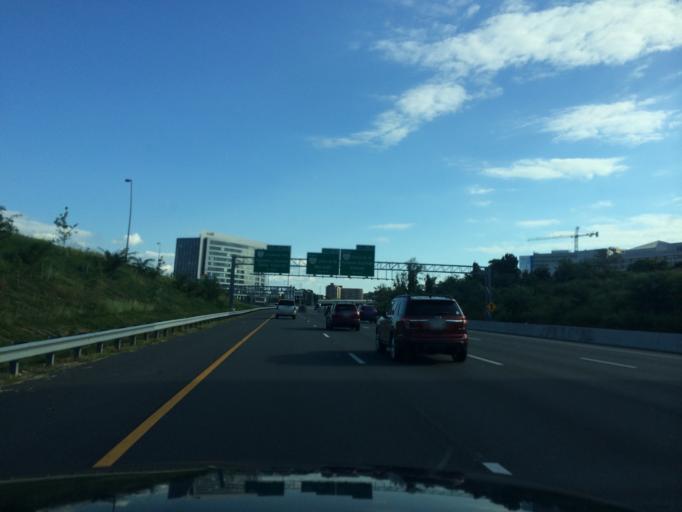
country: US
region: Virginia
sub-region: Fairfax County
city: Tysons Corner
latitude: 38.9288
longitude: -77.2143
